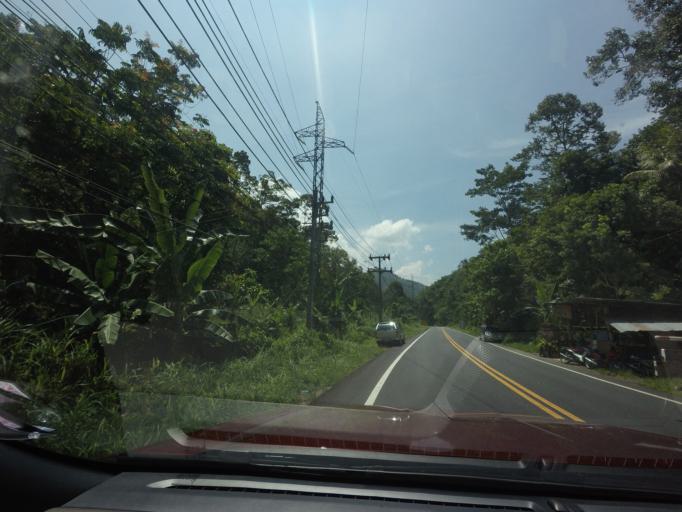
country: TH
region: Yala
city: Betong
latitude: 5.9138
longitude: 101.1560
